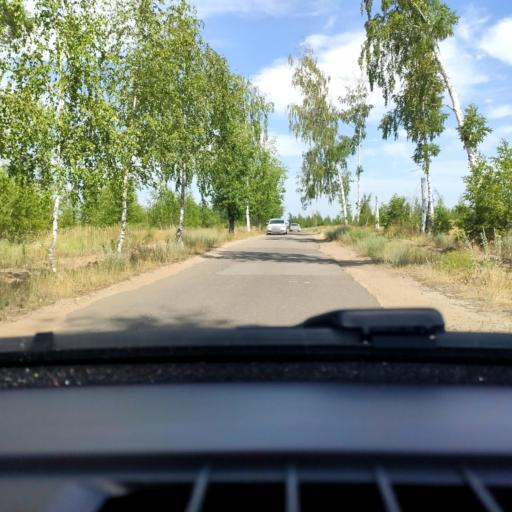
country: RU
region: Voronezj
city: Somovo
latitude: 51.7645
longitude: 39.3125
